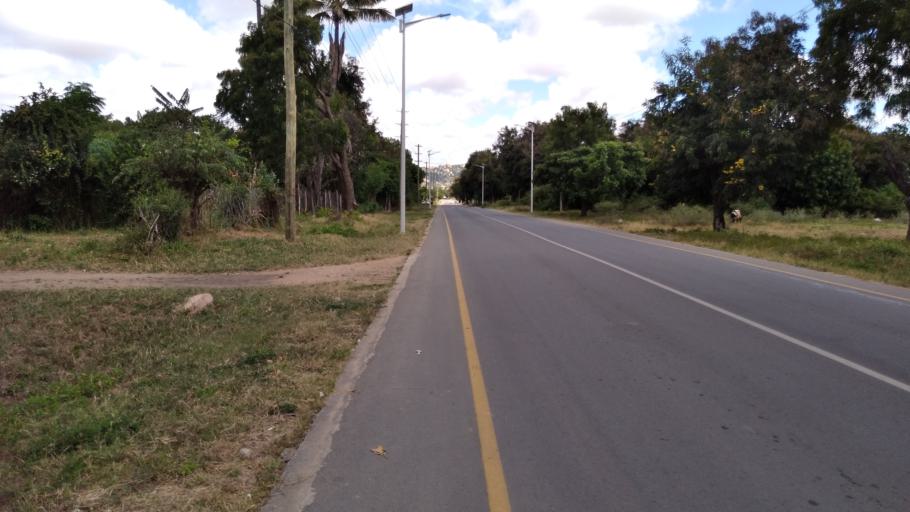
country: TZ
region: Dodoma
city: Dodoma
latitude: -6.1881
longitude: 35.7506
